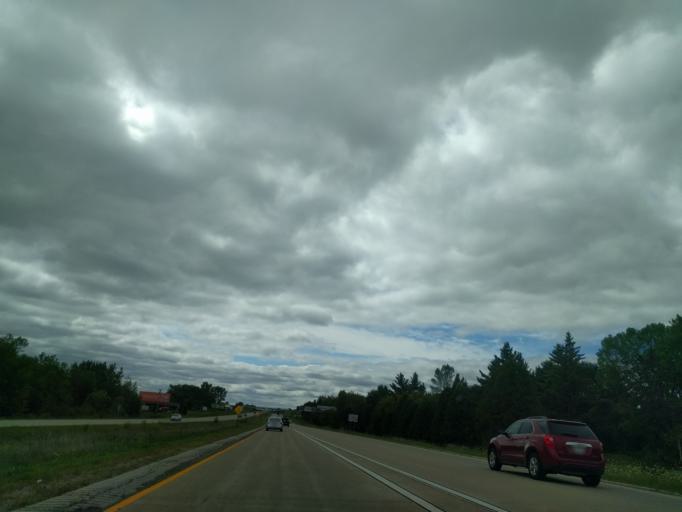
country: US
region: Wisconsin
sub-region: Oconto County
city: Oconto Falls
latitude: 44.7847
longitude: -88.0470
